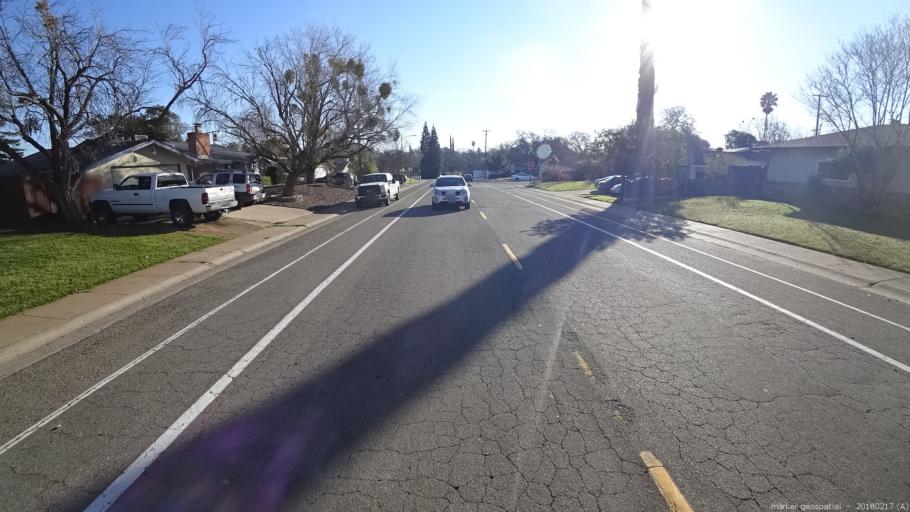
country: US
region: California
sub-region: Sacramento County
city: Folsom
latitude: 38.6712
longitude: -121.1987
